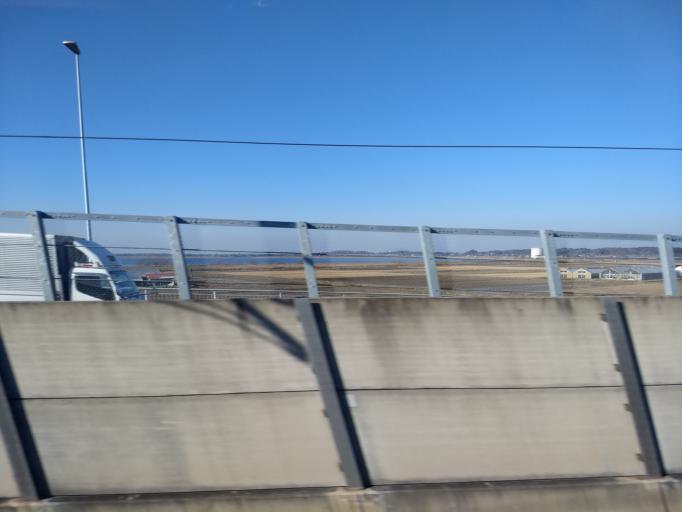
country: JP
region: Chiba
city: Narita
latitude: 35.7948
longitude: 140.2644
